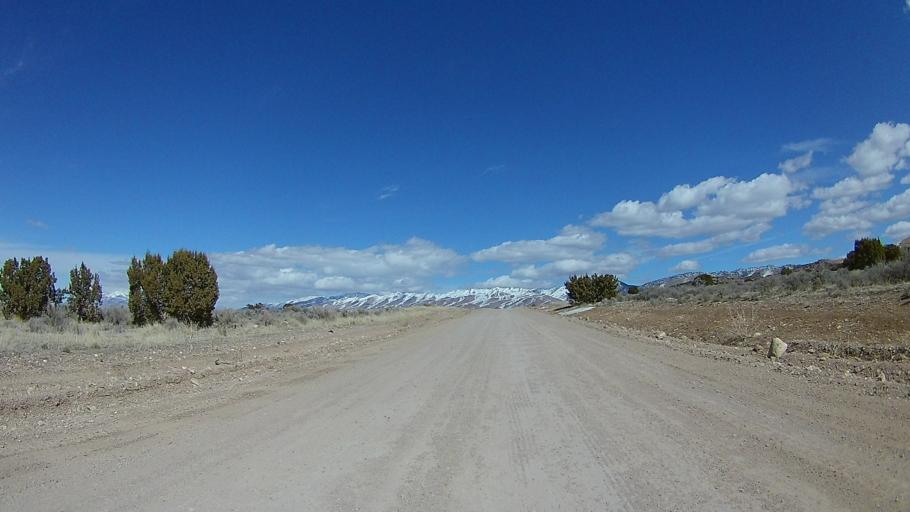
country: US
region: Utah
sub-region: Tooele County
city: Grantsville
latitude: 40.1136
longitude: -112.6472
